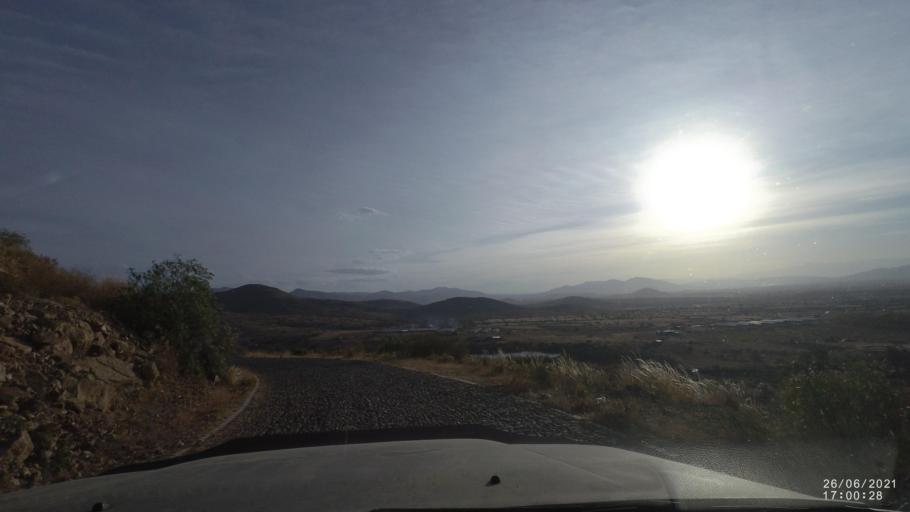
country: BO
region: Cochabamba
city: Cliza
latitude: -17.6604
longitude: -65.9075
